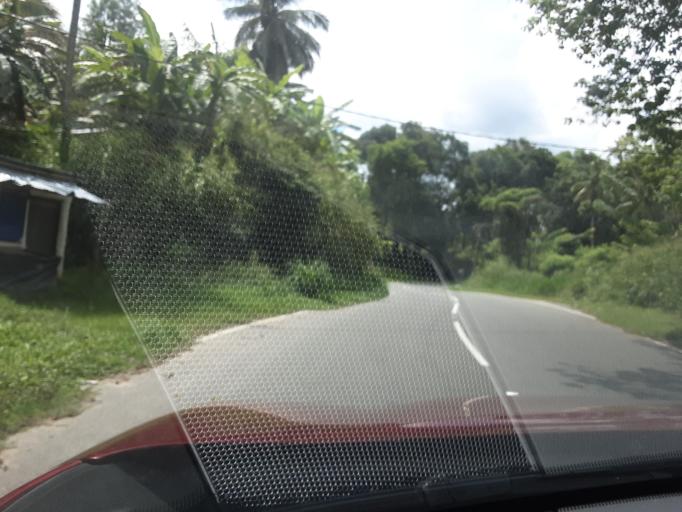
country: LK
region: Uva
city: Monaragala
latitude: 6.8974
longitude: 81.2775
